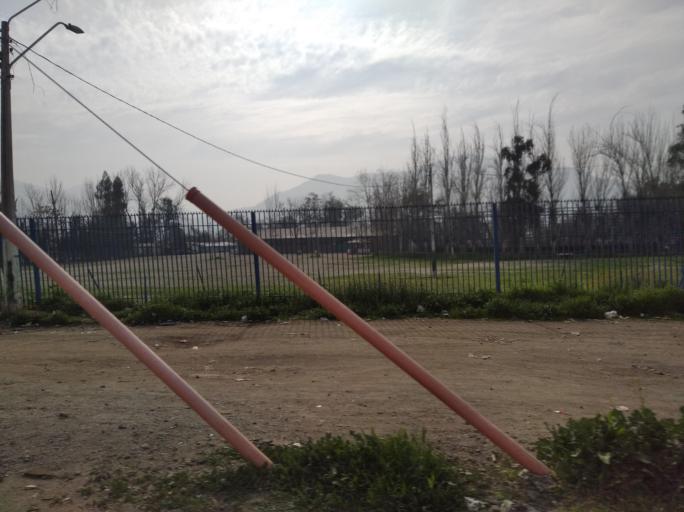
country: CL
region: Santiago Metropolitan
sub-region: Provincia de Chacabuco
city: Lampa
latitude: -33.2750
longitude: -70.8894
